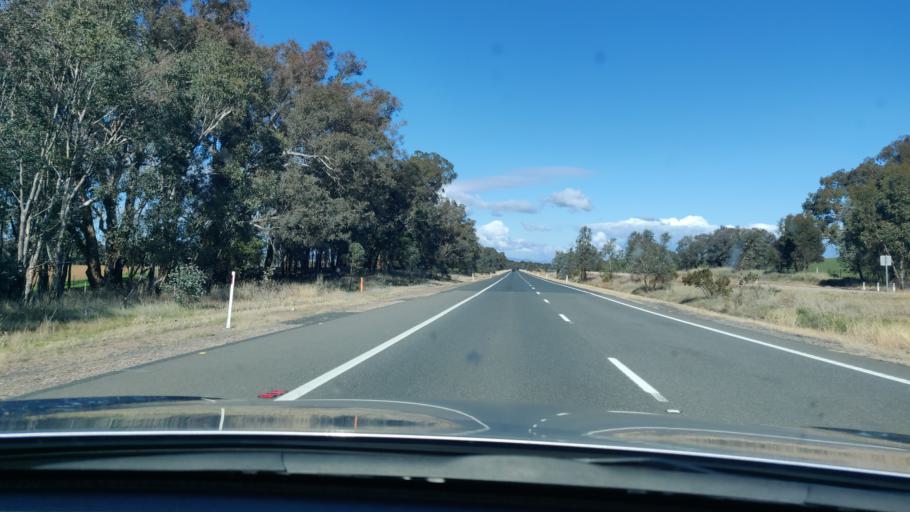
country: AU
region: New South Wales
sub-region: Greater Hume Shire
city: Holbrook
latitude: -35.5579
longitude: 147.5352
